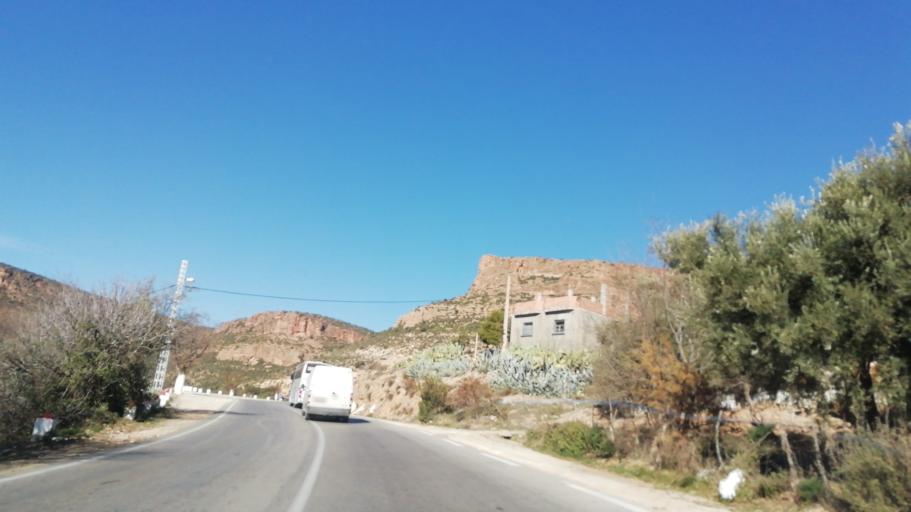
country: DZ
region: Tlemcen
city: Sebdou
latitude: 34.6851
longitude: -1.3176
